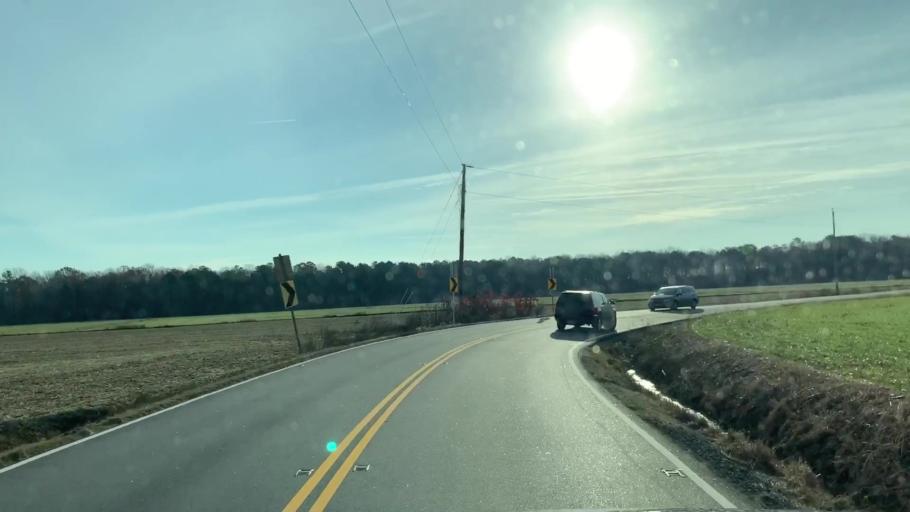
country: US
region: Virginia
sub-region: City of Virginia Beach
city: Virginia Beach
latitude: 36.7172
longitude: -76.0505
